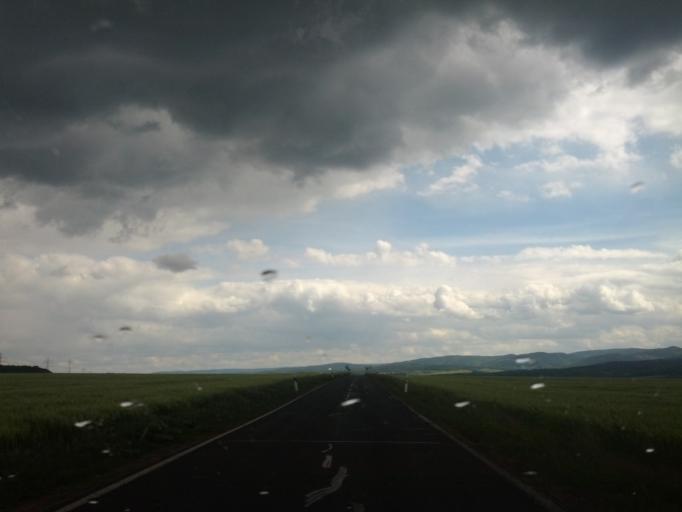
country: DE
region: Thuringia
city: Haina
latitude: 50.9685
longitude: 10.5095
